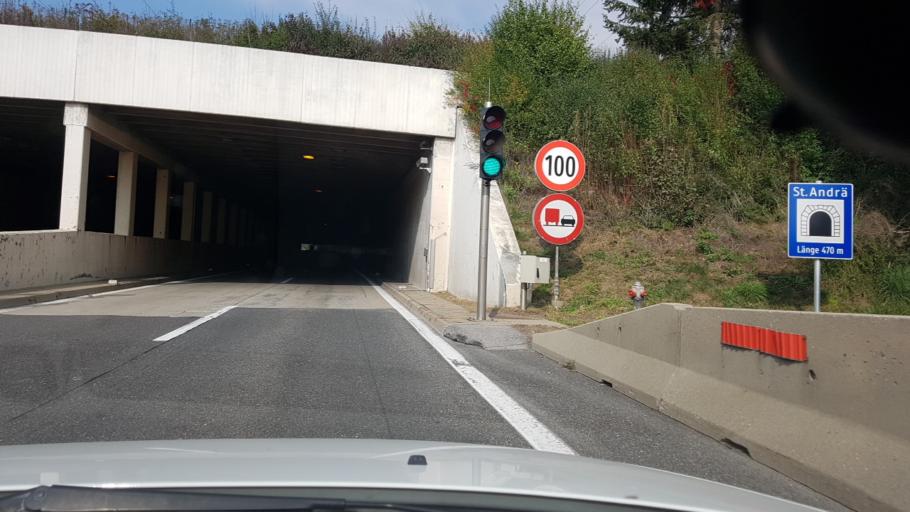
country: AT
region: Carinthia
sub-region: Villach Stadt
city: Villach
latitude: 46.6381
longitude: 13.8915
